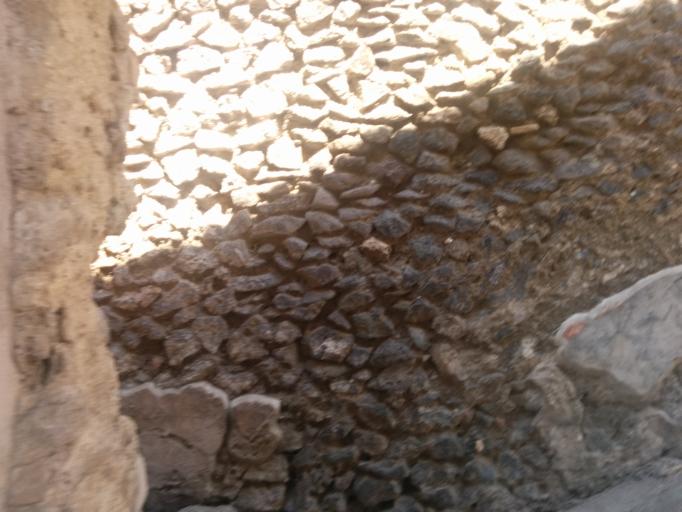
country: IT
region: Campania
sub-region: Provincia di Napoli
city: Pompei
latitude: 40.7510
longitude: 14.4869
